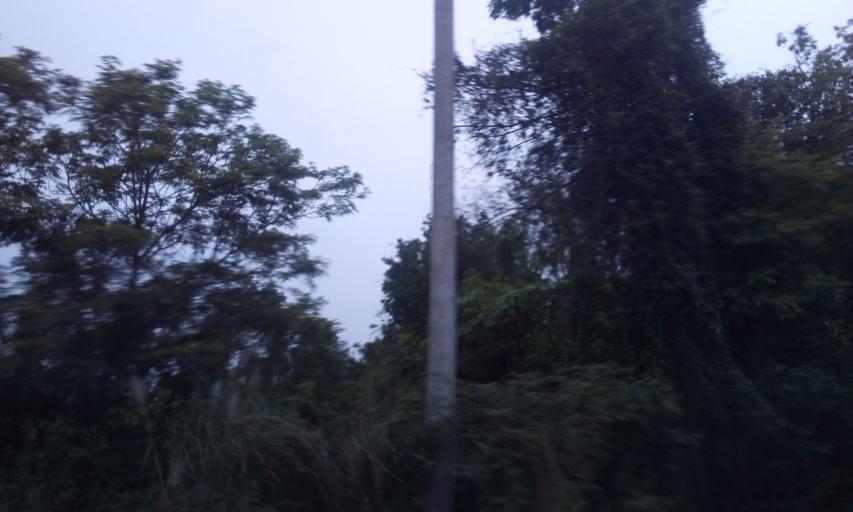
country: TH
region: Chachoengsao
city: Plaeng Yao
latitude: 13.5705
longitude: 101.2645
